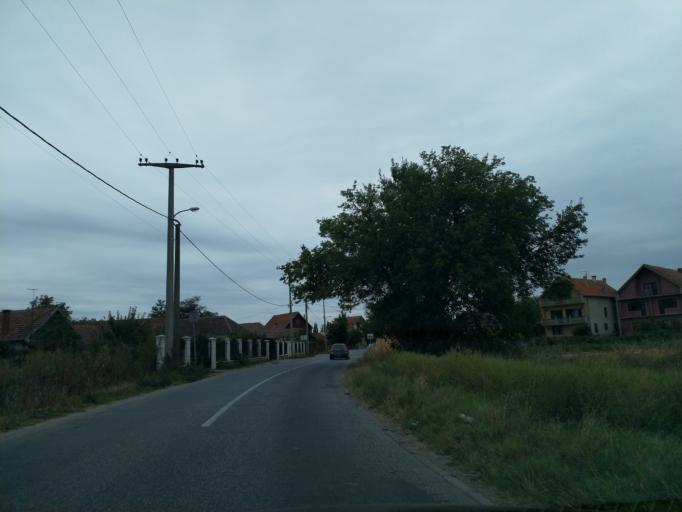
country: RS
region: Central Serbia
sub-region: Pomoravski Okrug
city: Paracin
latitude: 43.8530
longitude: 21.3926
